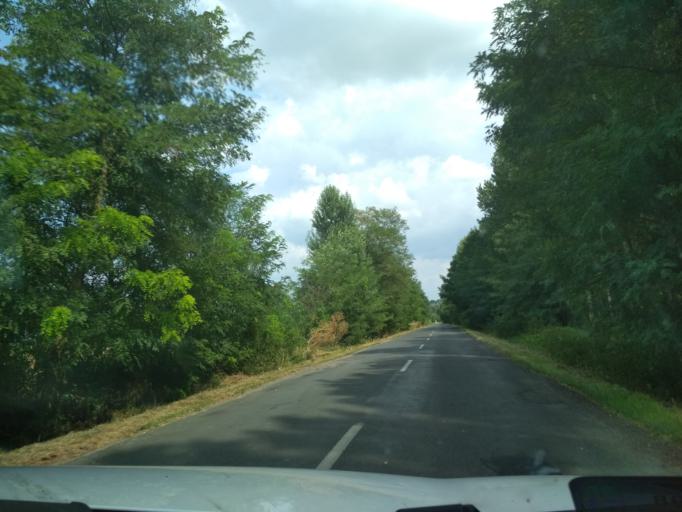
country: HU
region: Jasz-Nagykun-Szolnok
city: Tiszaszolos
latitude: 47.5243
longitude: 20.6757
